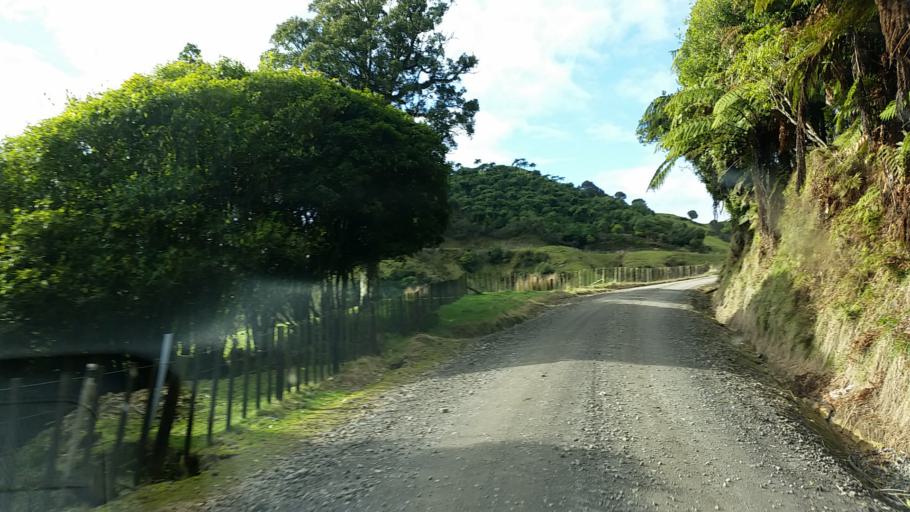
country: NZ
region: Taranaki
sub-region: South Taranaki District
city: Eltham
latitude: -39.1737
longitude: 174.6158
